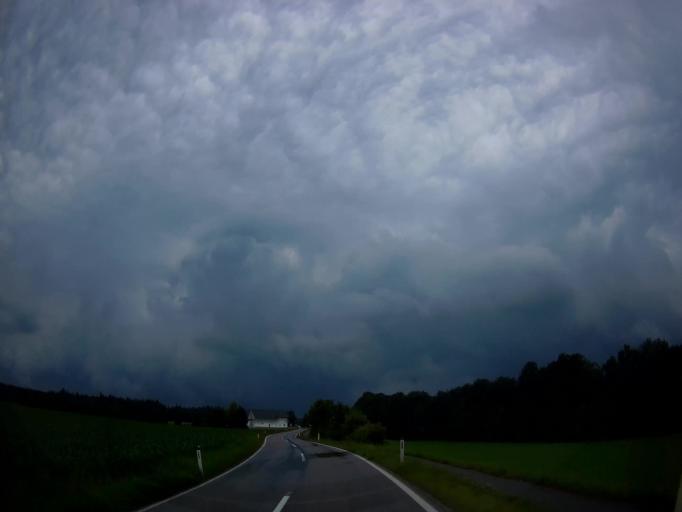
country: AT
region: Salzburg
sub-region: Politischer Bezirk Salzburg-Umgebung
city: Mattsee
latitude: 48.0451
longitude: 13.1493
